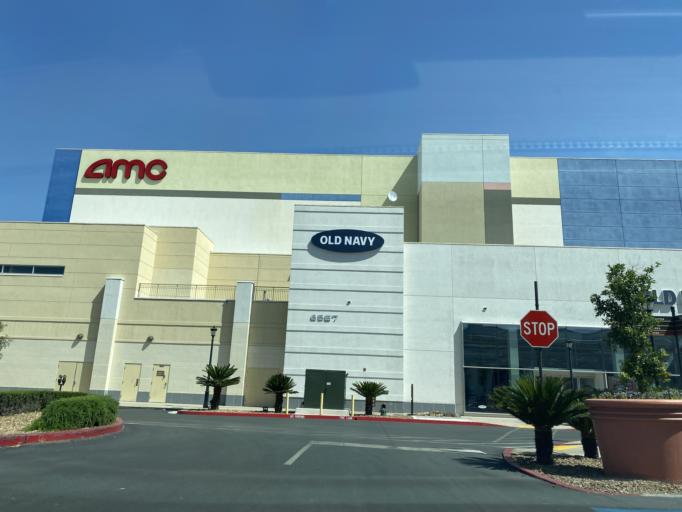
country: US
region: Nevada
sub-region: Clark County
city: Paradise
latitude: 36.0672
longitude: -115.1786
